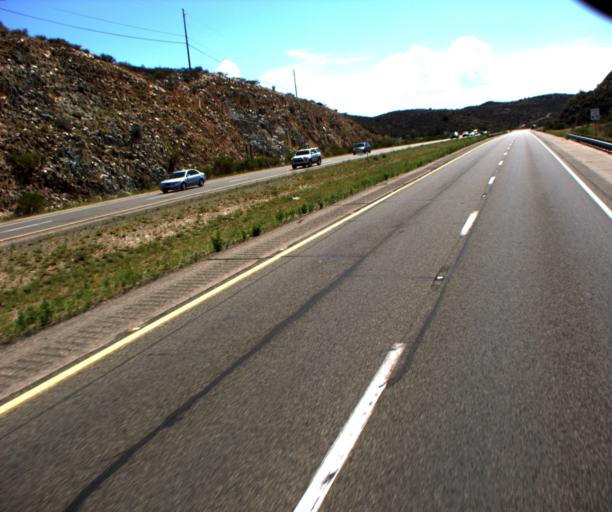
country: US
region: Arizona
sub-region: Yavapai County
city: Mayer
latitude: 34.3818
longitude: -112.2030
